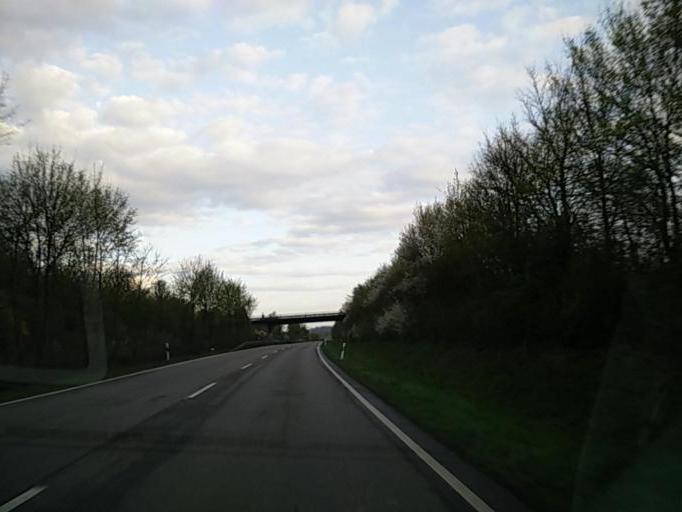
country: DE
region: Baden-Wuerttemberg
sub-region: Regierungsbezirk Stuttgart
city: Herrenberg
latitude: 48.5739
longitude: 8.9162
